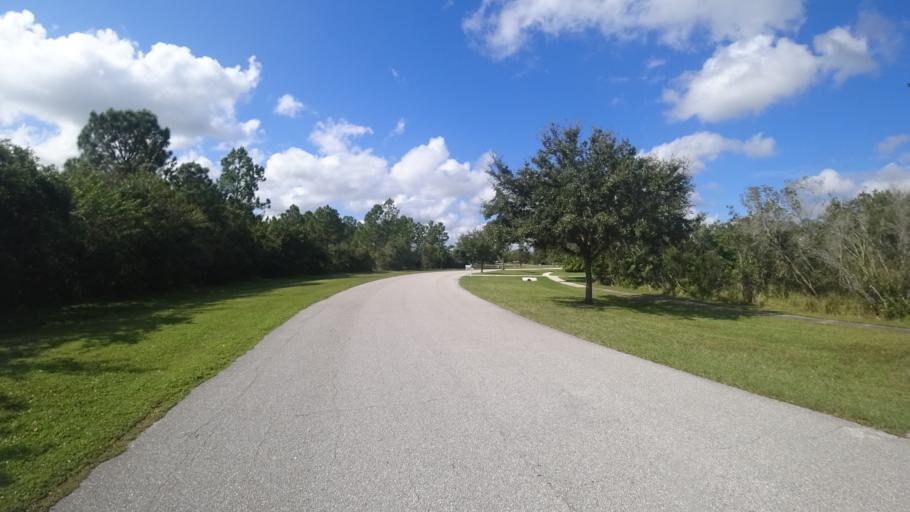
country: US
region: Florida
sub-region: Sarasota County
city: Fruitville
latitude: 27.3953
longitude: -82.3122
